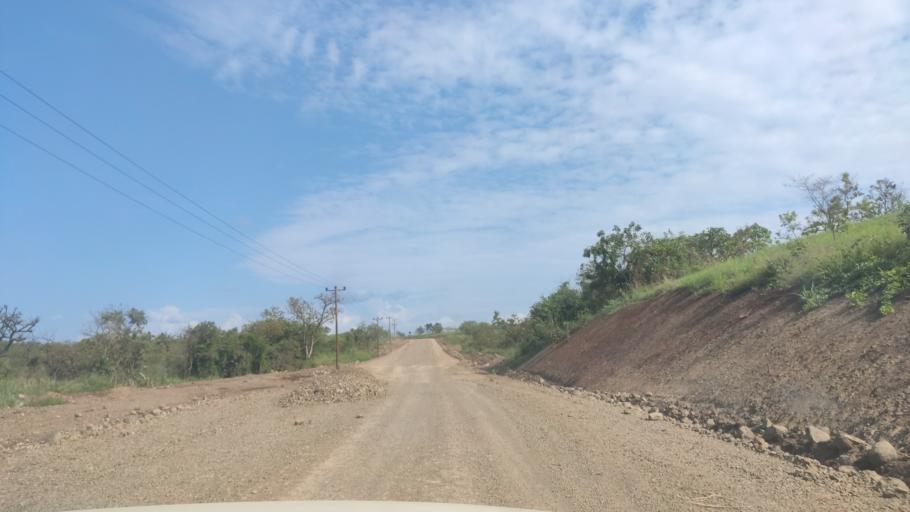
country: ET
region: Southern Nations, Nationalities, and People's Region
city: Felege Neway
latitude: 6.4262
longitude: 37.2175
